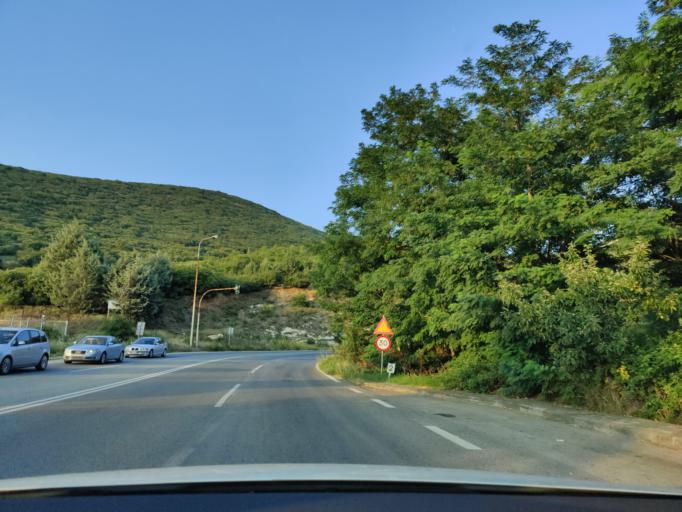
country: GR
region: East Macedonia and Thrace
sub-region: Nomos Kavalas
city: Amygdaleonas
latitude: 40.9510
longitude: 24.3708
